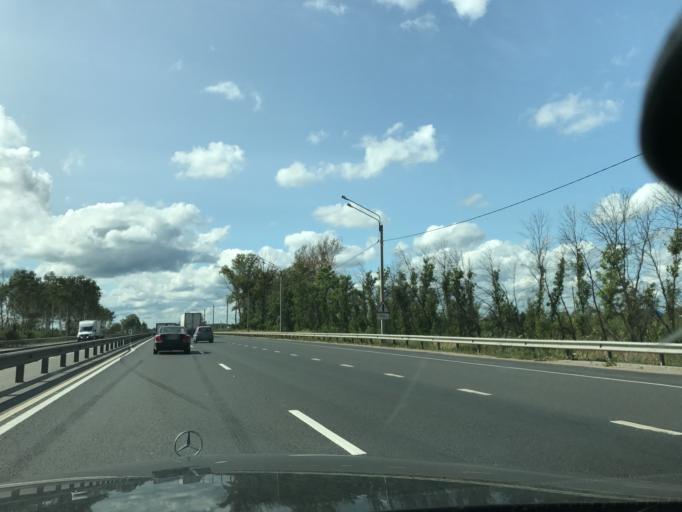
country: RU
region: Vladimir
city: Vyazniki
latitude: 56.2397
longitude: 42.0977
